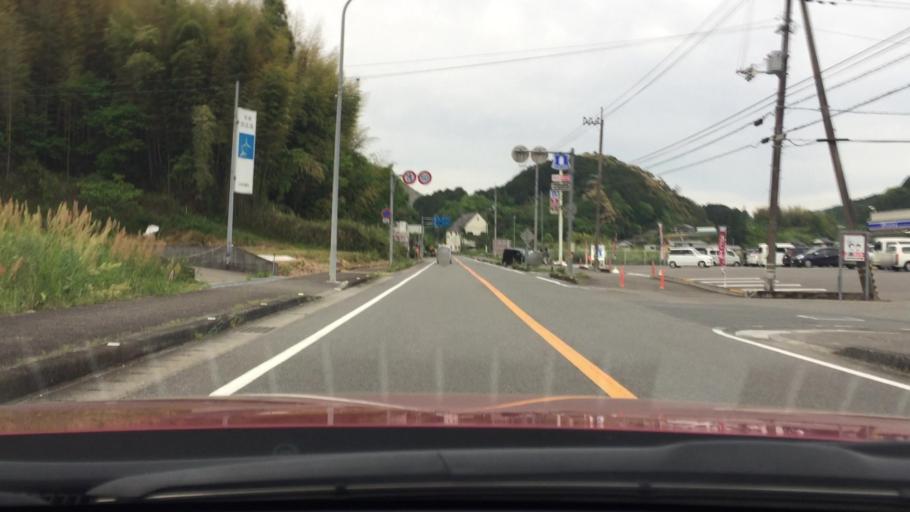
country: JP
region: Kochi
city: Ino
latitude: 33.5268
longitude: 133.3462
